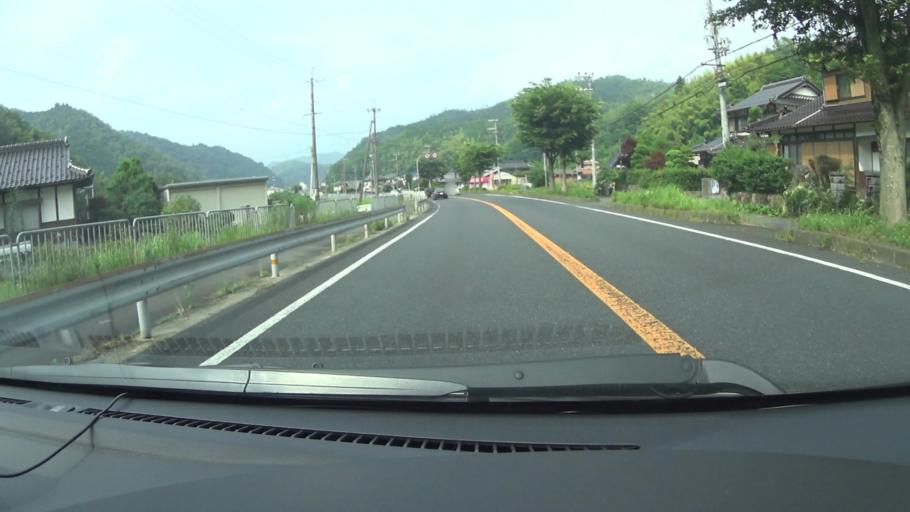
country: JP
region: Kyoto
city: Maizuru
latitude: 35.4709
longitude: 135.3657
